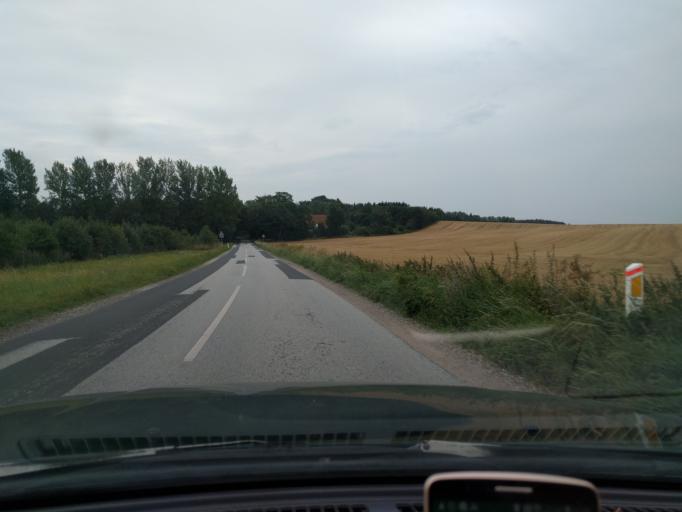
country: DK
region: Zealand
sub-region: Slagelse Kommune
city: Skaelskor
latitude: 55.2840
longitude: 11.2685
